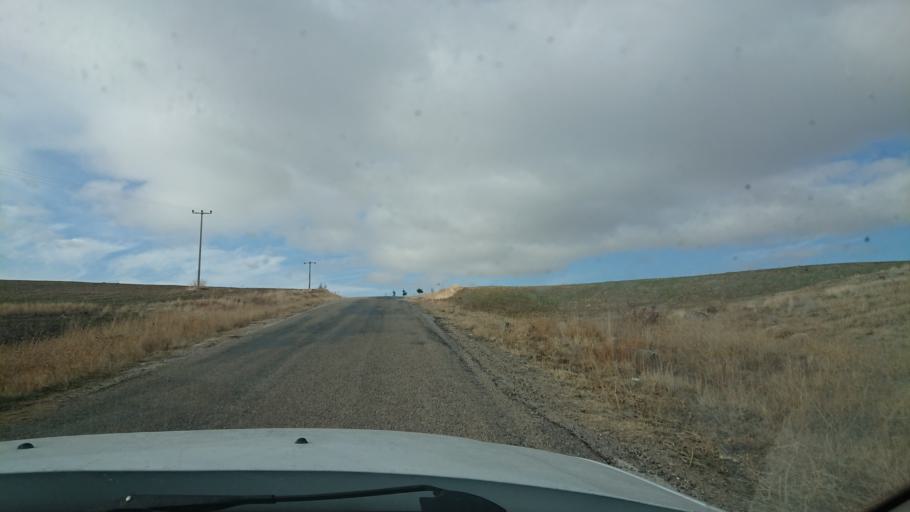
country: TR
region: Aksaray
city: Agacoren
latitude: 38.8198
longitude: 33.9666
